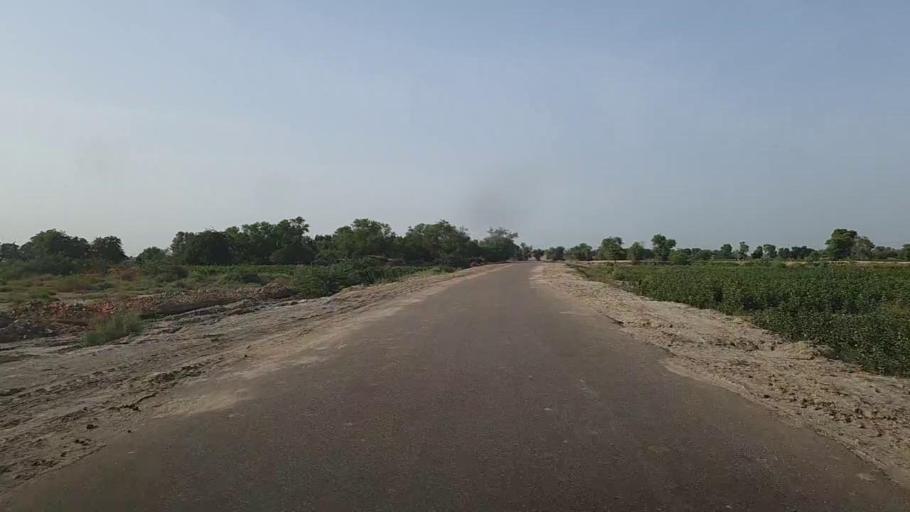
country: PK
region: Sindh
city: Ubauro
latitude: 28.0985
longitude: 69.8455
